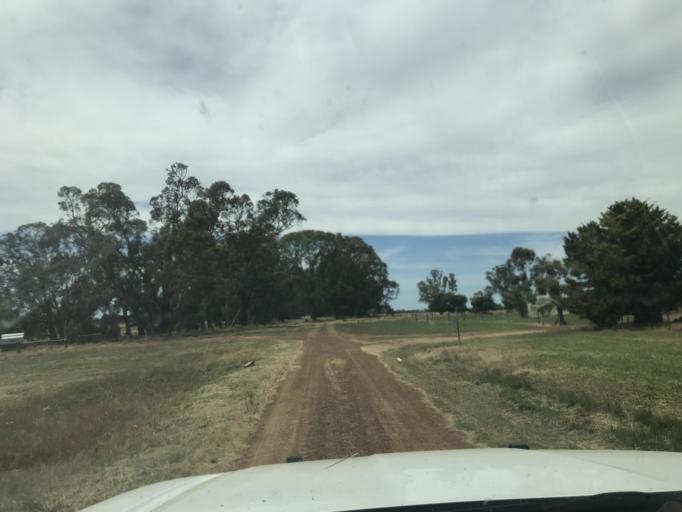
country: AU
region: South Australia
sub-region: Wattle Range
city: Penola
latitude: -37.0275
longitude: 141.4922
